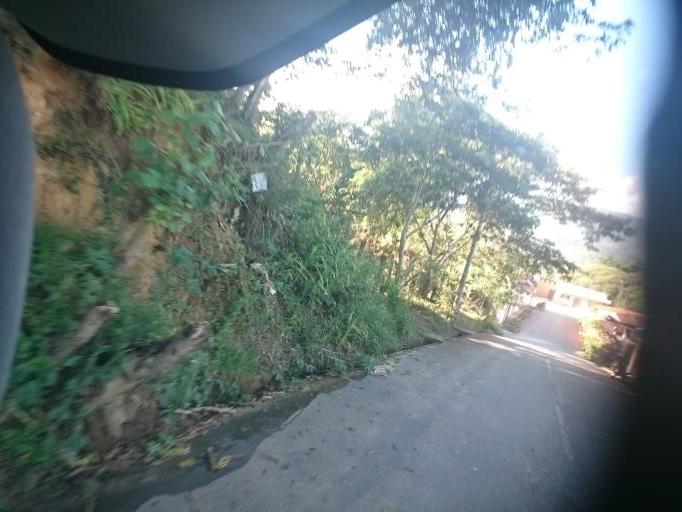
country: PE
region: San Martin
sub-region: Provincia de Lamas
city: Lamas
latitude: -6.4184
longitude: -76.5234
